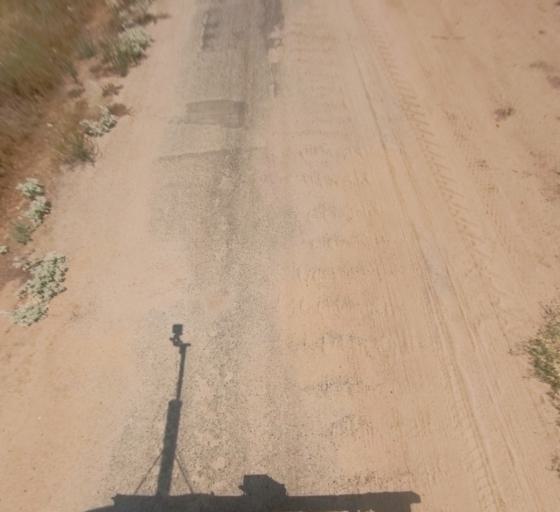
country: US
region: California
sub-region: Madera County
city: Fairmead
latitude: 37.1468
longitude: -120.1382
